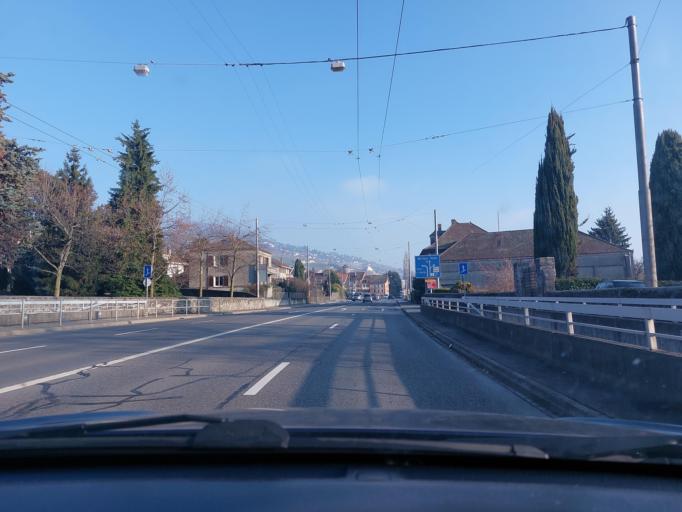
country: CH
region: Vaud
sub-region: Lavaux-Oron District
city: Lutry
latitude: 46.5043
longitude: 6.6837
